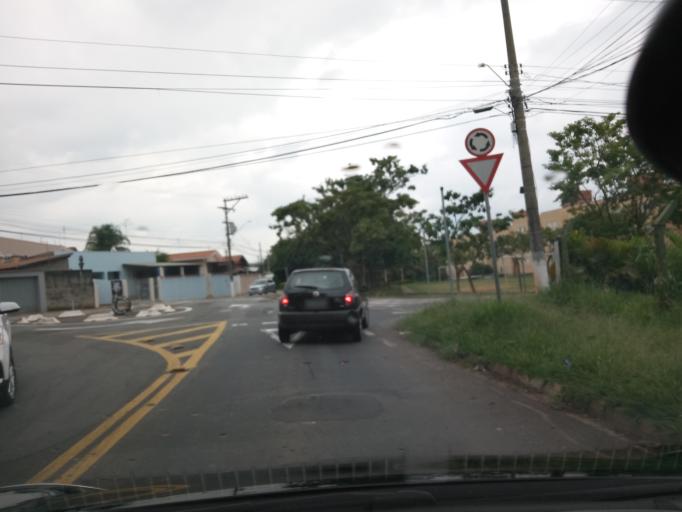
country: BR
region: Sao Paulo
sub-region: Campinas
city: Campinas
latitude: -22.8816
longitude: -47.0413
